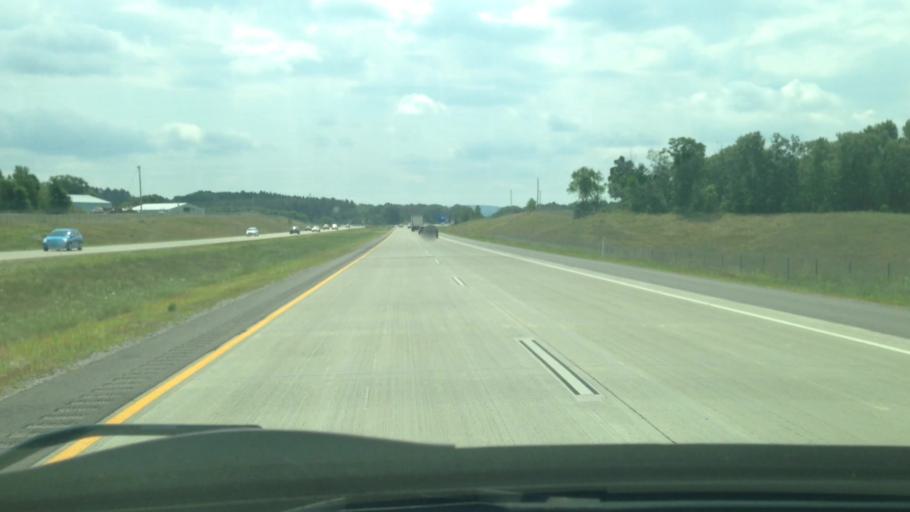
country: US
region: Wisconsin
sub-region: Sauk County
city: West Baraboo
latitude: 43.4893
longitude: -89.7793
